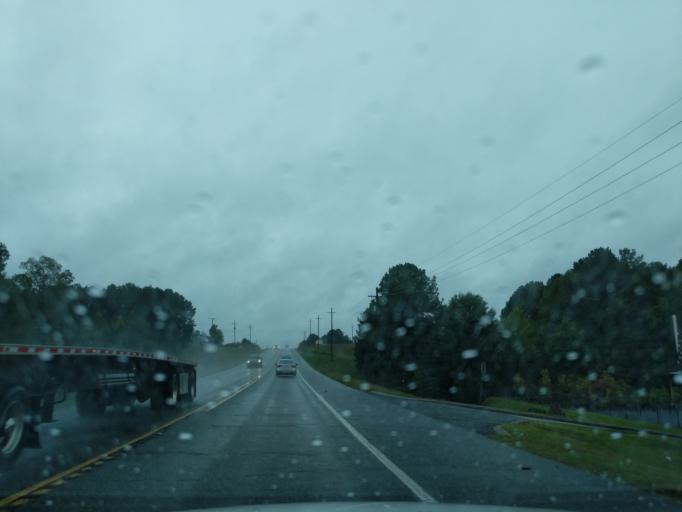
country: US
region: Louisiana
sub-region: Webster Parish
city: Minden
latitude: 32.6129
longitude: -93.2498
